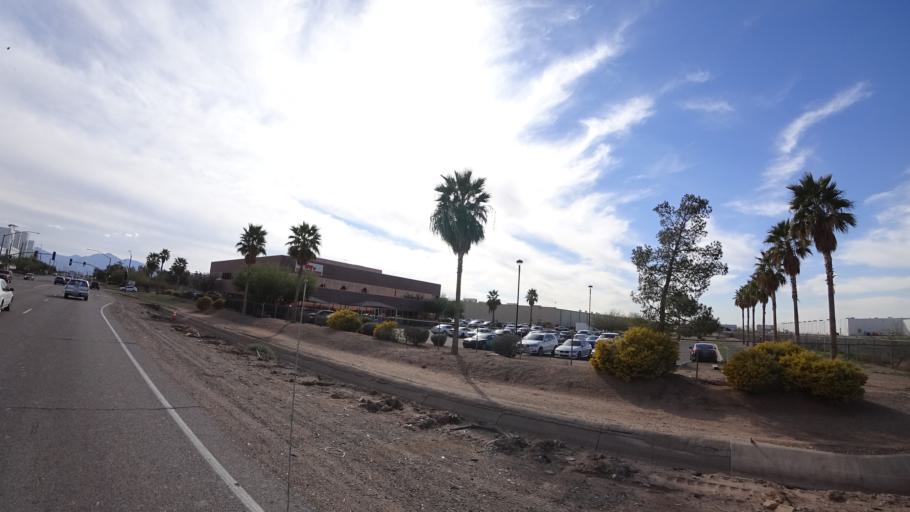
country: US
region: Arizona
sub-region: Maricopa County
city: Tolleson
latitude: 33.4428
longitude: -112.2725
